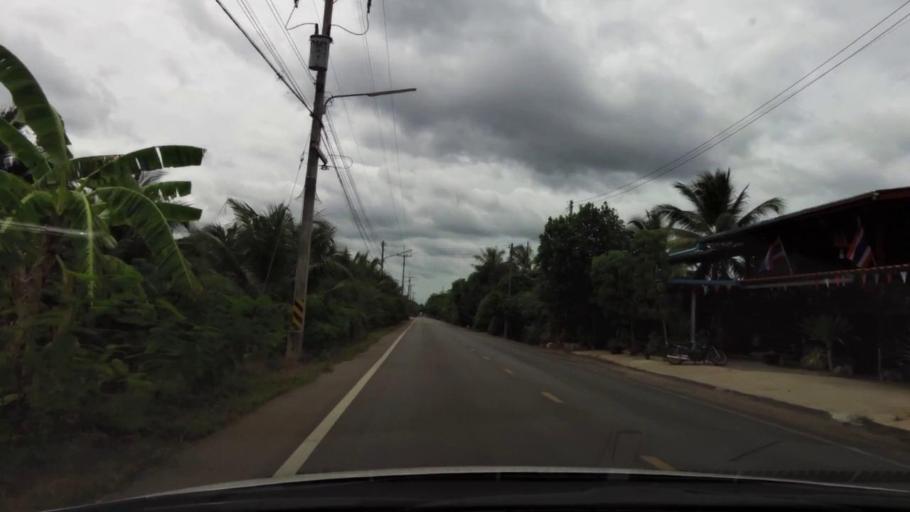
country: TH
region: Ratchaburi
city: Damnoen Saduak
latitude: 13.5528
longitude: 100.0167
